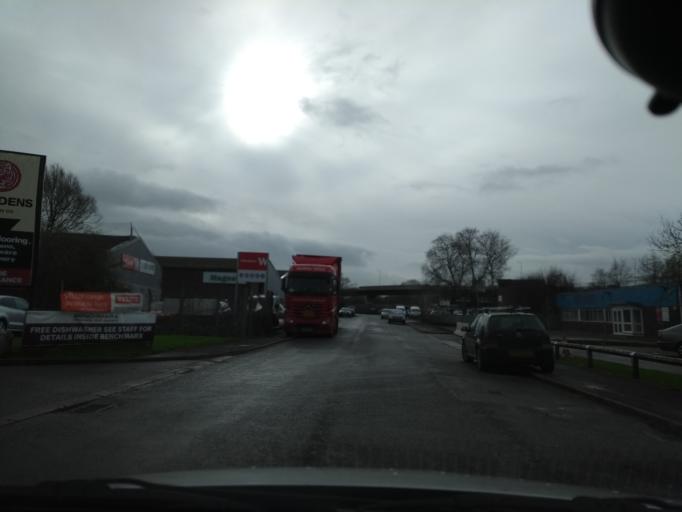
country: GB
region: England
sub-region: Somerset
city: Taunton
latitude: 51.0256
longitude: -3.0873
